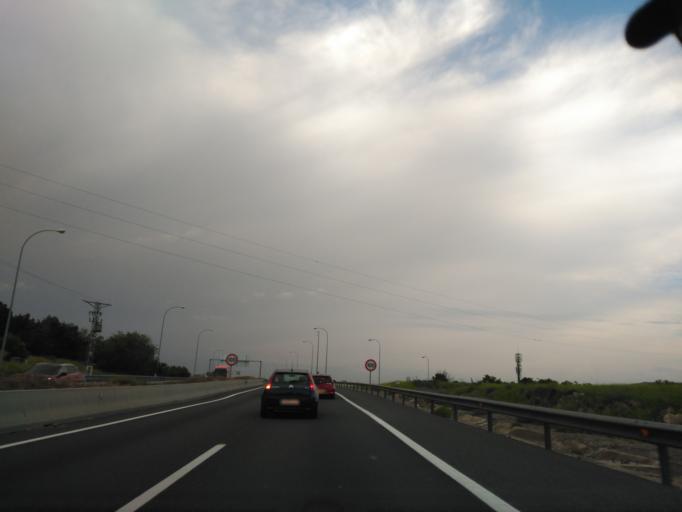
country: ES
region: Madrid
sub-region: Provincia de Madrid
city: Villaverde
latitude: 40.3426
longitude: -3.6727
